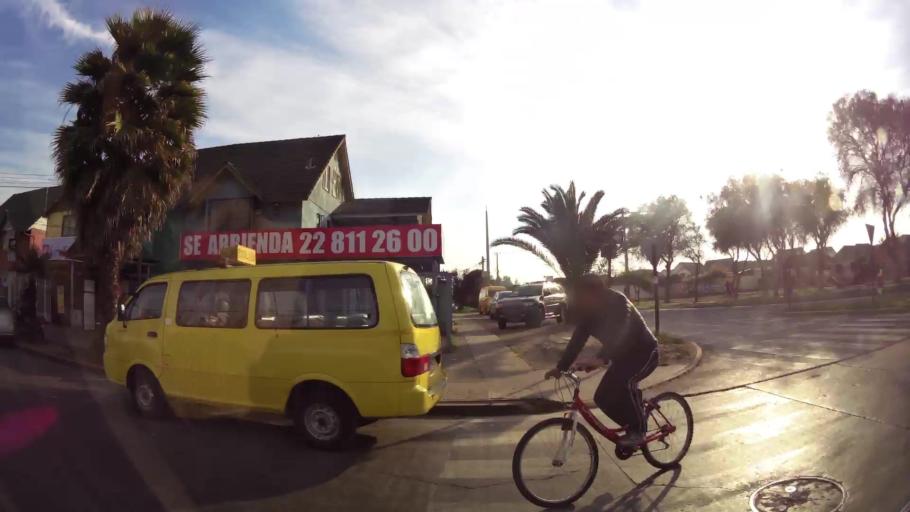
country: CL
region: Santiago Metropolitan
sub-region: Provincia de Maipo
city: San Bernardo
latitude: -33.5611
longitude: -70.7858
